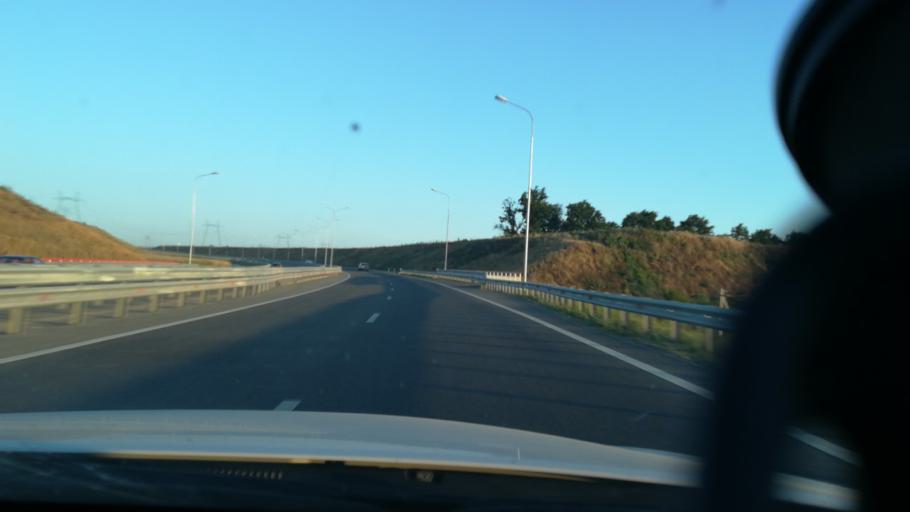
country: RU
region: Krasnodarskiy
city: Dzhiginka
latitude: 45.1265
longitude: 37.3107
